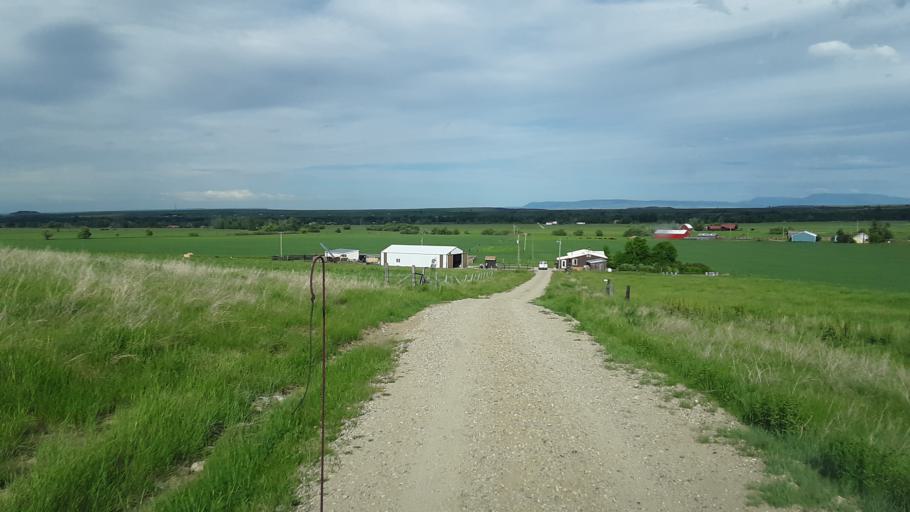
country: US
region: Montana
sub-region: Carbon County
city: Red Lodge
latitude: 45.3718
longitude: -109.1878
